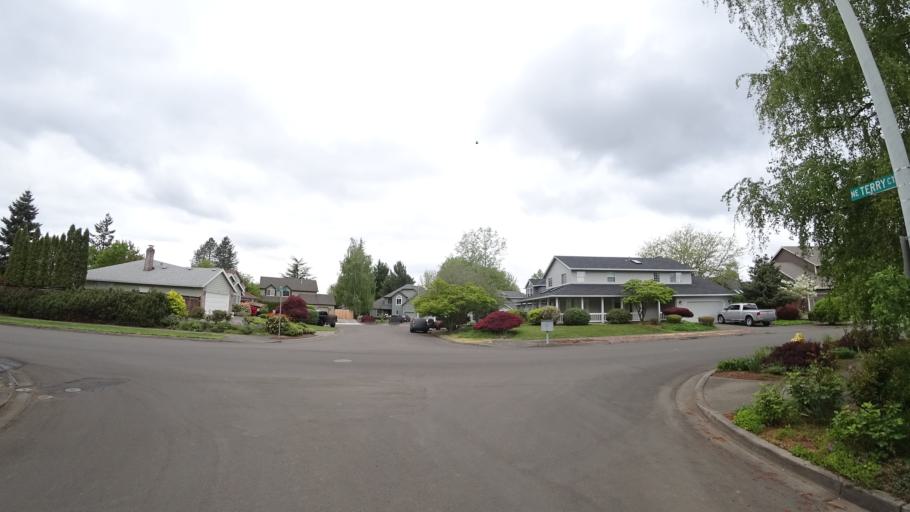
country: US
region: Oregon
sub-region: Washington County
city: Hillsboro
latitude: 45.5395
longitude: -122.9809
